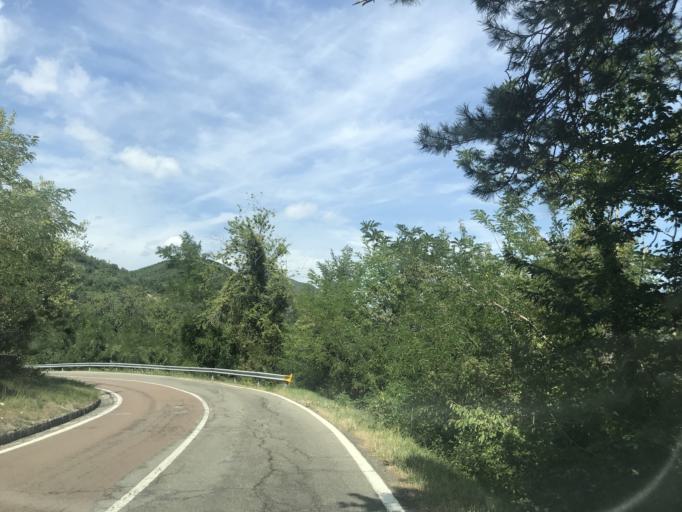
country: IT
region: Emilia-Romagna
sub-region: Provincia di Bologna
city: Grizzana
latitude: 44.2566
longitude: 11.1616
